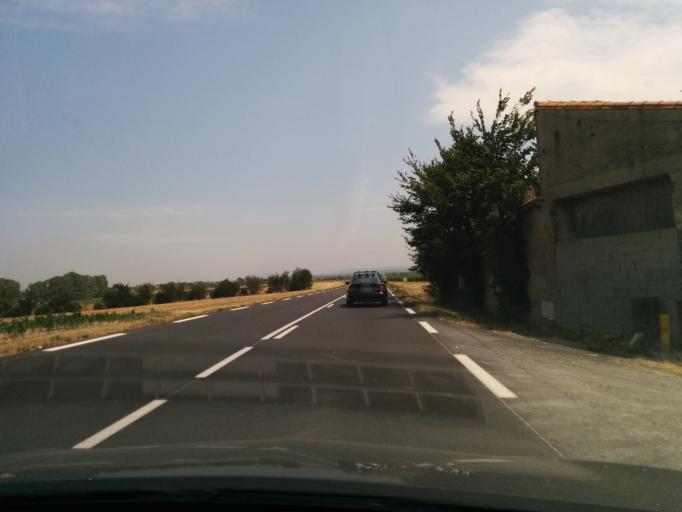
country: FR
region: Languedoc-Roussillon
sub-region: Departement de l'Aude
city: Bram
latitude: 43.2593
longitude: 2.1417
